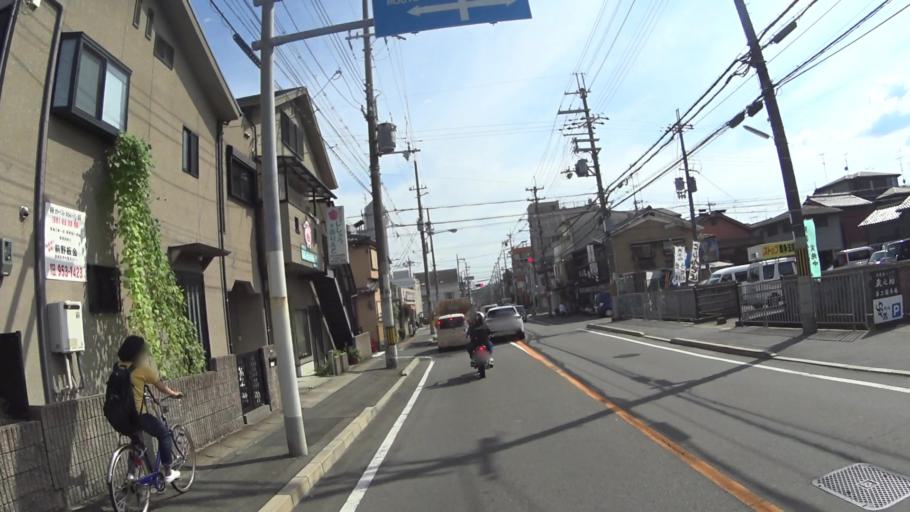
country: JP
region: Kyoto
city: Muko
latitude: 34.9738
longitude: 135.6942
